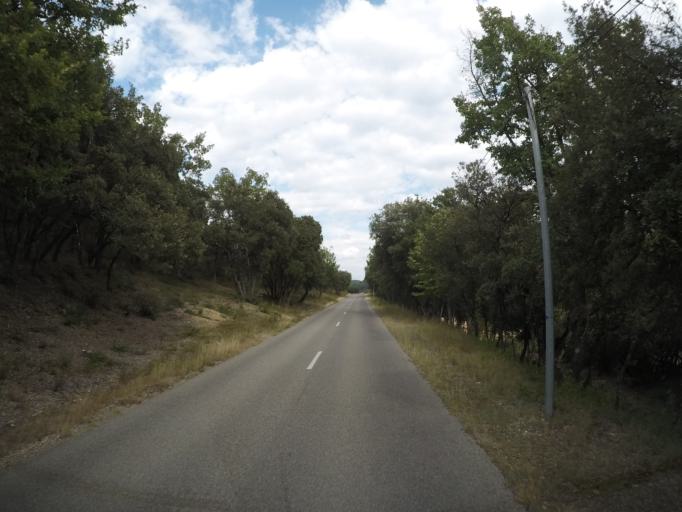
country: FR
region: Provence-Alpes-Cote d'Azur
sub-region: Departement des Alpes-de-Haute-Provence
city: Greoux-les-Bains
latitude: 43.7793
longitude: 5.9082
